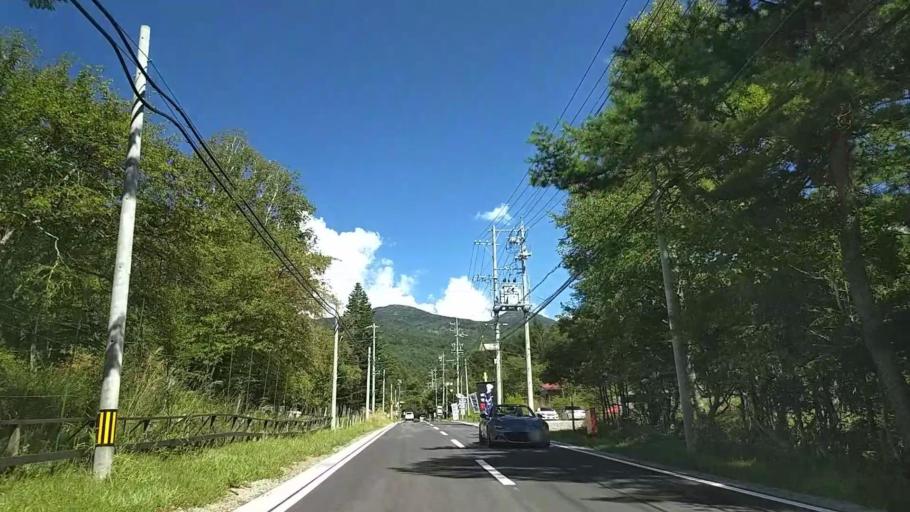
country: JP
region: Nagano
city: Chino
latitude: 36.0628
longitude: 138.2807
